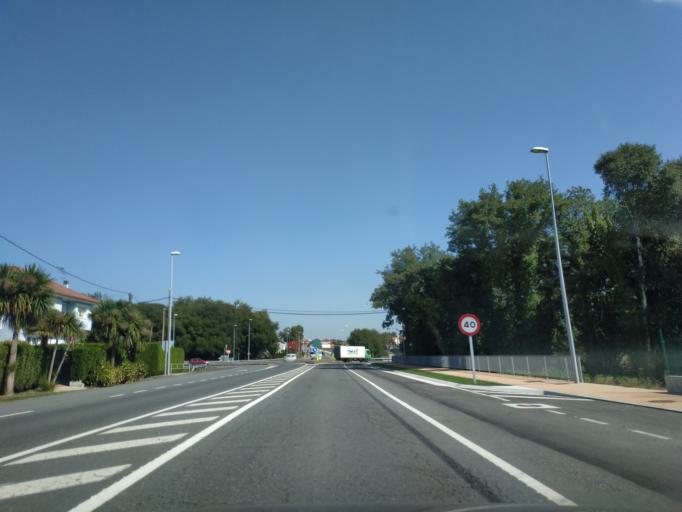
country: ES
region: Galicia
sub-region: Provincia da Coruna
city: Laracha
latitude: 43.2515
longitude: -8.6110
